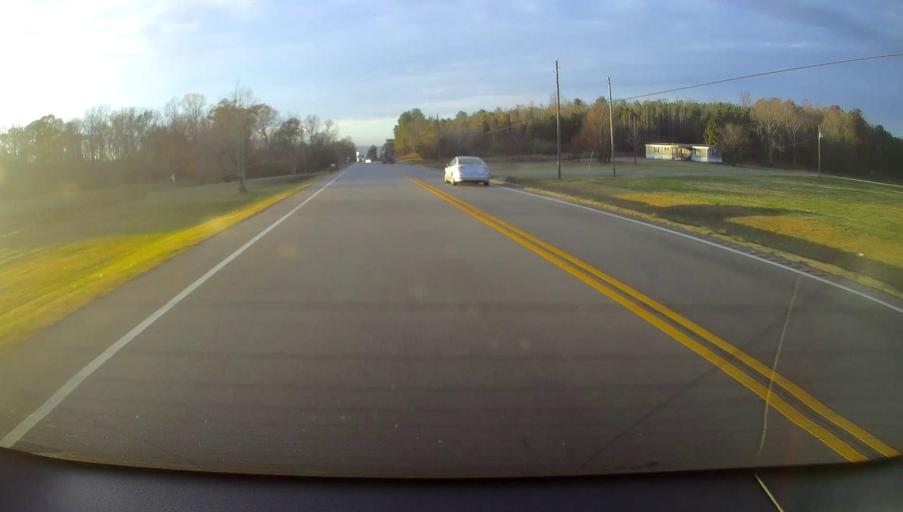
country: US
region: Alabama
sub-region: Saint Clair County
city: Steele
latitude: 34.0633
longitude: -86.2423
